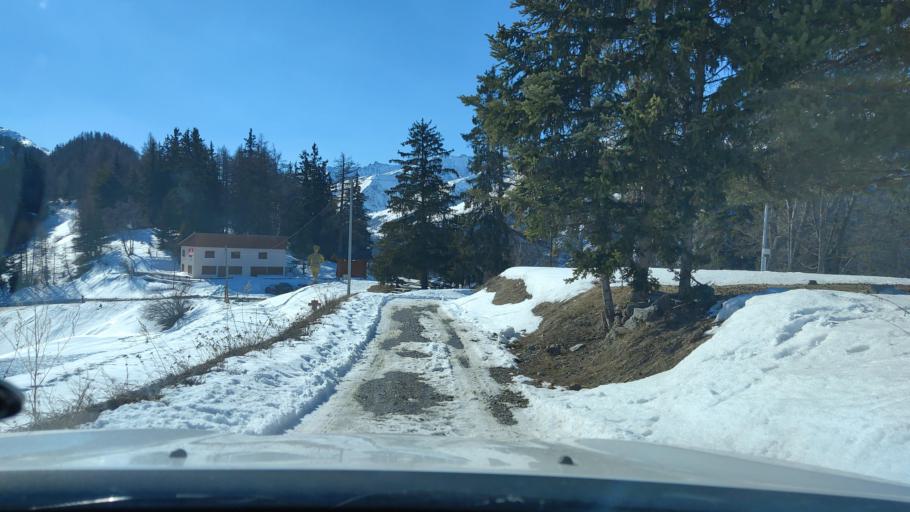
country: FR
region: Rhone-Alpes
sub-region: Departement de la Savoie
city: Saint-Michel-de-Maurienne
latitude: 45.2035
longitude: 6.4451
